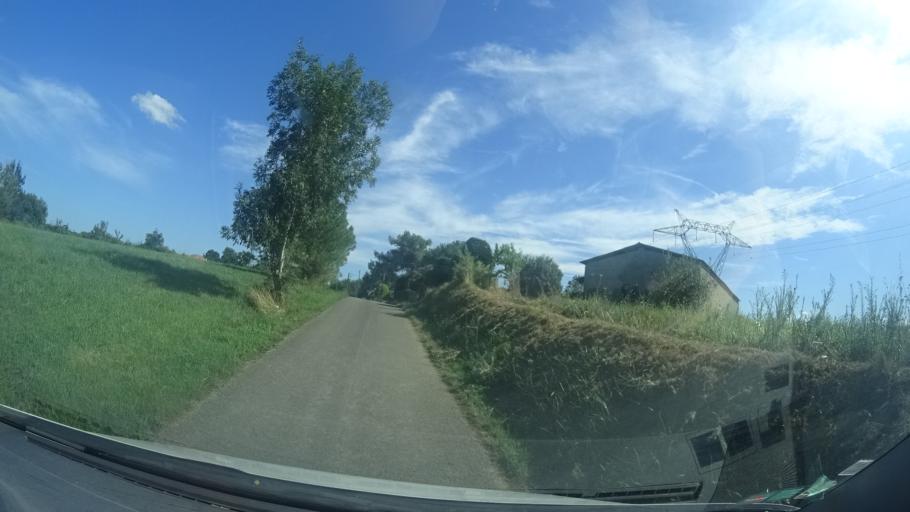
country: FR
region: Aquitaine
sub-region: Departement des Pyrenees-Atlantiques
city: Mont
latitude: 43.5032
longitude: -0.6784
